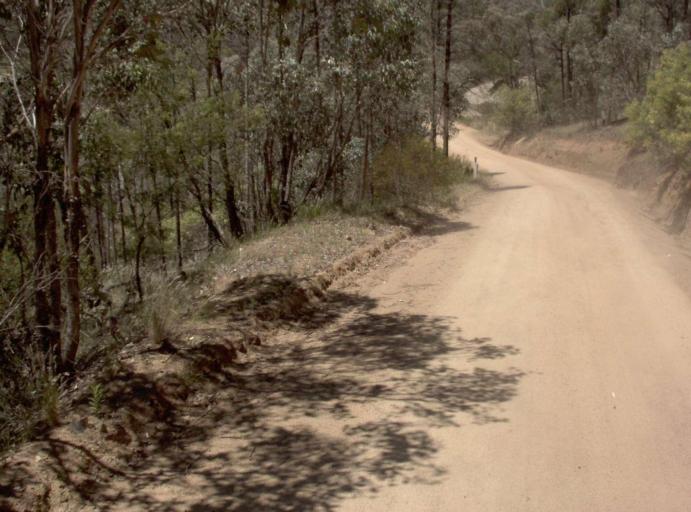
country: AU
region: New South Wales
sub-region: Snowy River
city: Jindabyne
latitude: -36.9120
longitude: 148.4196
